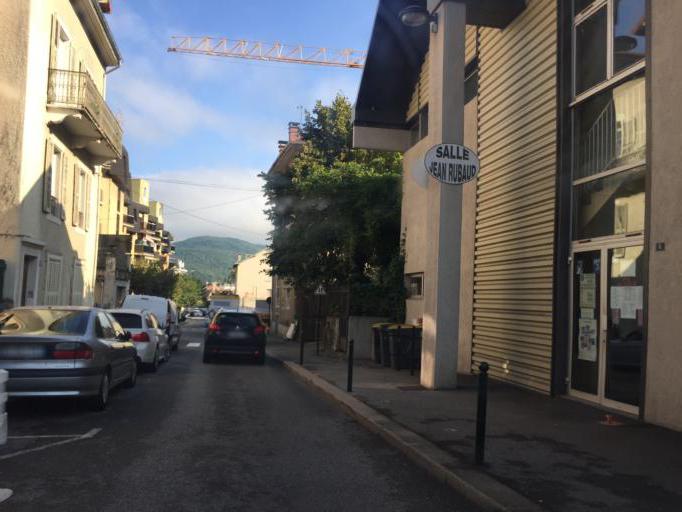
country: FR
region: Rhone-Alpes
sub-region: Departement de la Savoie
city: Aix-les-Bains
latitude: 45.6927
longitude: 5.9138
